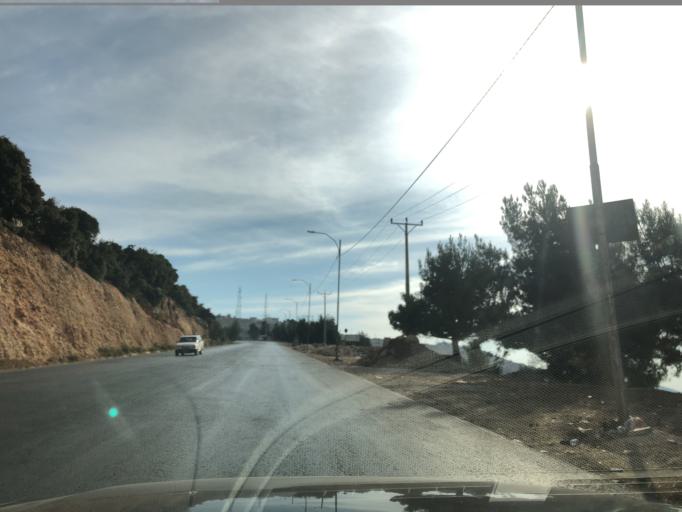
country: JO
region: Irbid
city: `Anjarah
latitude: 32.3078
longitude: 35.7770
